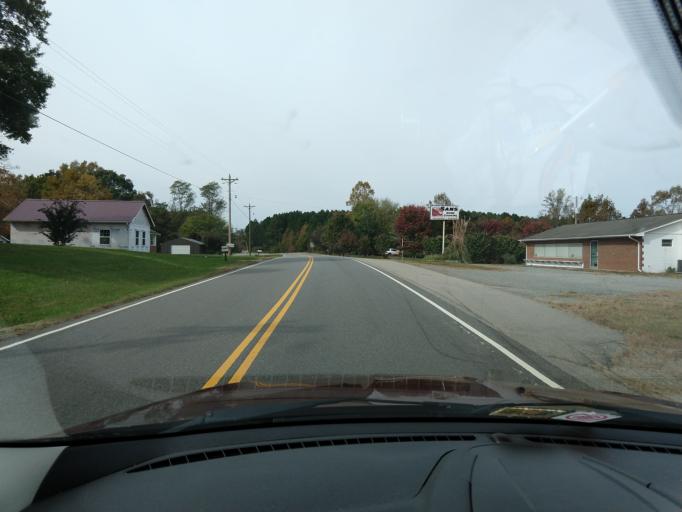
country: US
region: Virginia
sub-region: Franklin County
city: Union Hall
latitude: 36.9563
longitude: -79.5379
